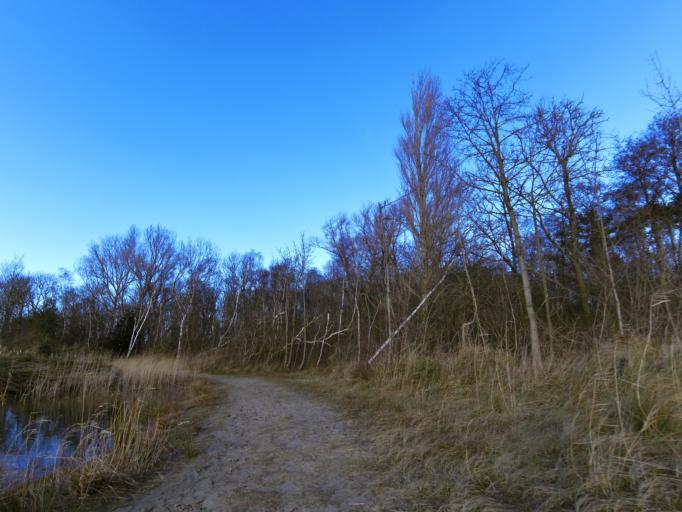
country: NL
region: South Holland
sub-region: Gemeente Goeree-Overflakkee
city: Goedereede
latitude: 51.8859
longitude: 4.0460
